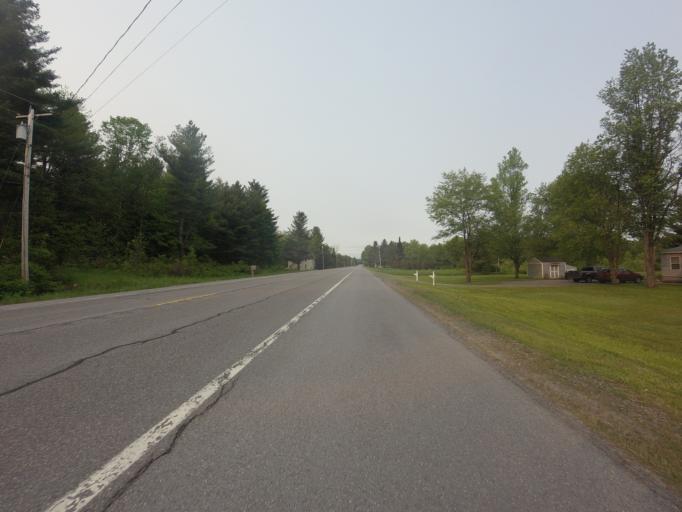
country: US
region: New York
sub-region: Jefferson County
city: Carthage
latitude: 44.0856
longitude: -75.4319
